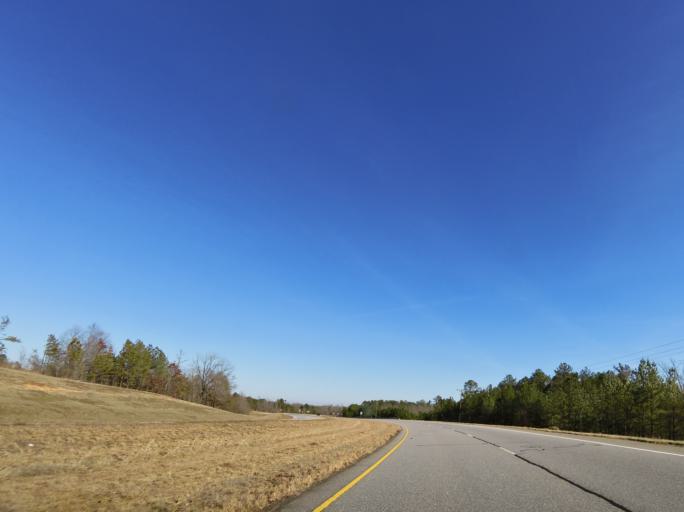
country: US
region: Georgia
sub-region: Upson County
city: Thomaston
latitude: 32.7442
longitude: -84.2324
